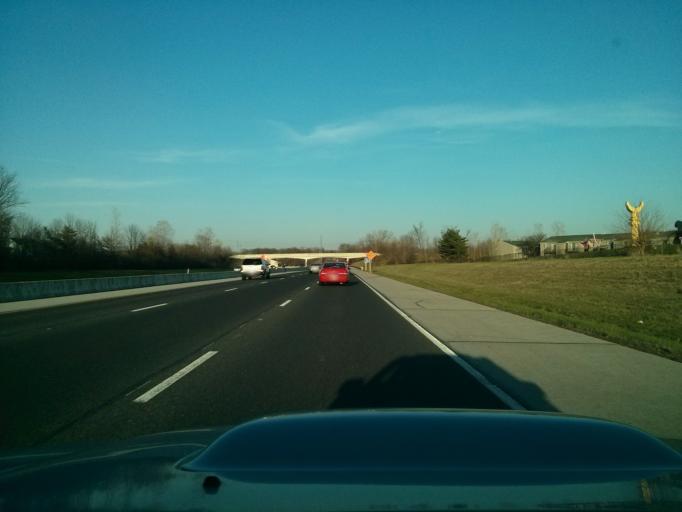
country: US
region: Indiana
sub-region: Marion County
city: Meridian Hills
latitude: 39.9243
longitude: -86.1876
